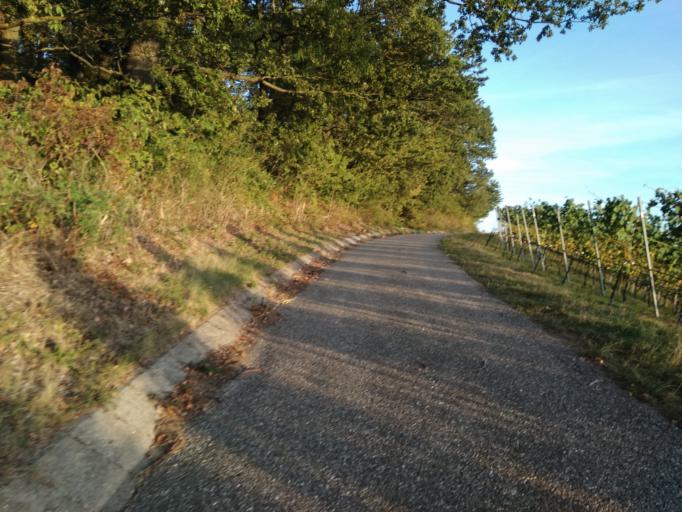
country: DE
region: Baden-Wuerttemberg
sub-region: Regierungsbezirk Stuttgart
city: Weinsberg
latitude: 49.1585
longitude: 9.2749
